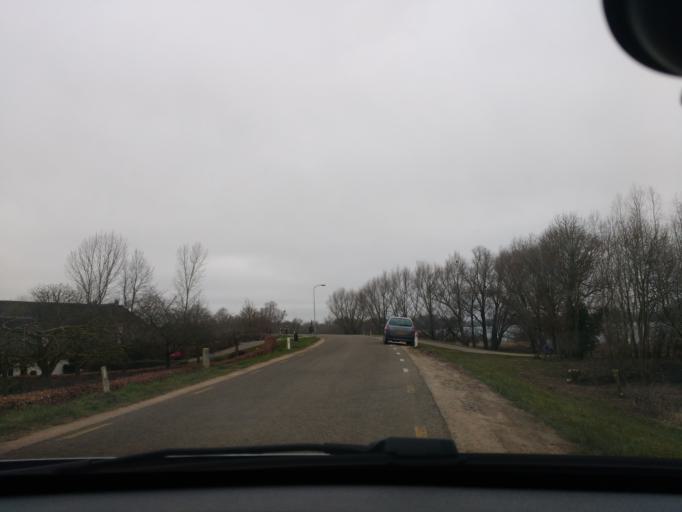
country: NL
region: Gelderland
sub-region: Gemeente Groesbeek
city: Berg en Dal
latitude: 51.8634
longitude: 5.9349
